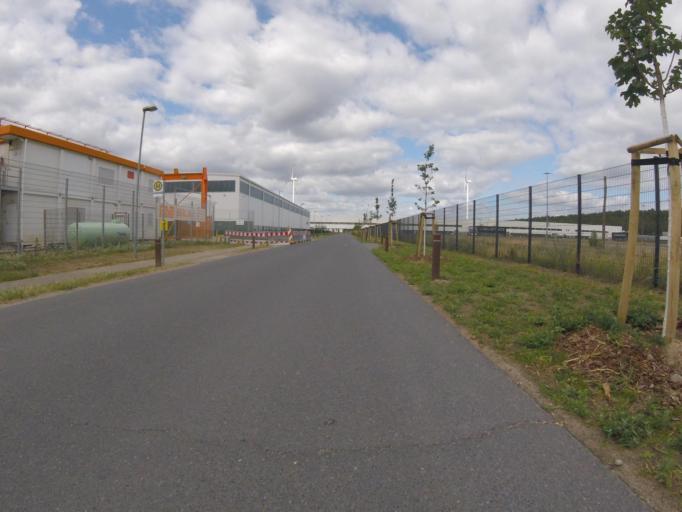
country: DE
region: Brandenburg
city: Wildau
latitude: 52.3199
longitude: 13.6736
